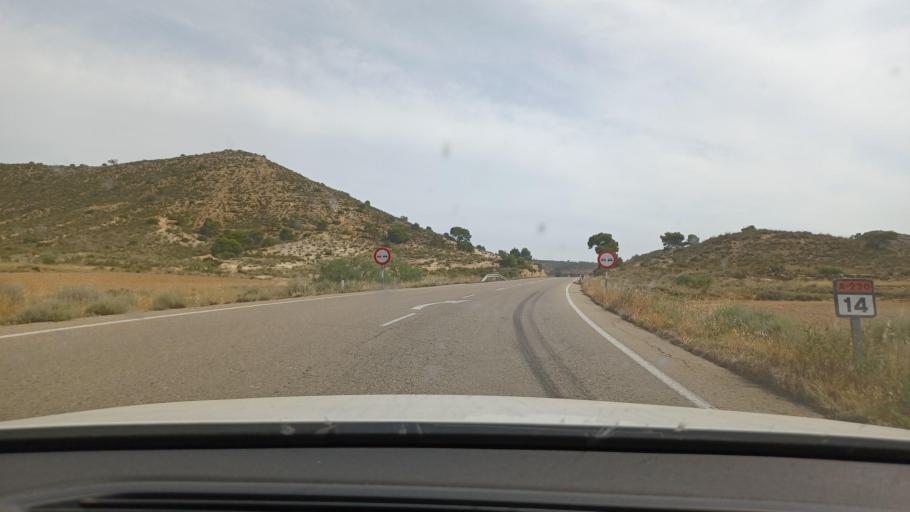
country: ES
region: Aragon
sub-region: Provincia de Zaragoza
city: Chiprana
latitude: 41.3388
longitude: -0.0898
